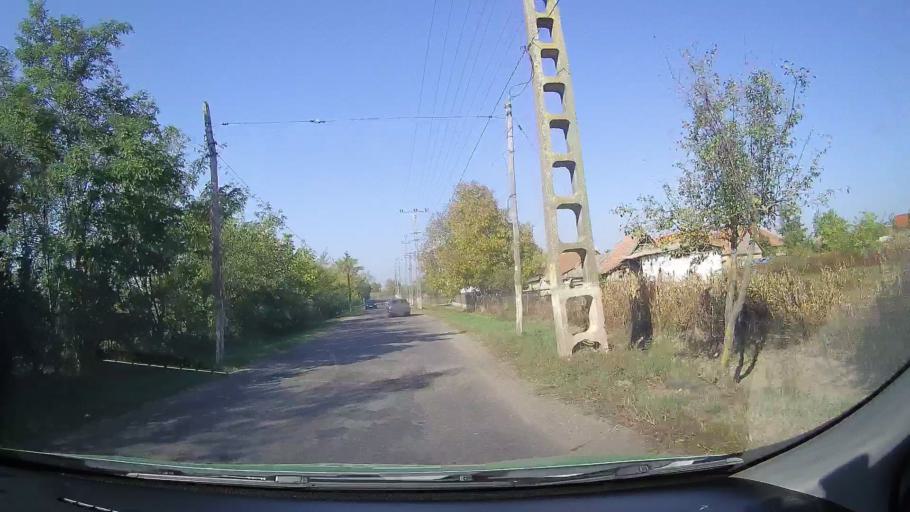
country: RO
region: Satu Mare
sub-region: Comuna Sanislau
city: Sanislau
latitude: 47.6329
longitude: 22.3292
